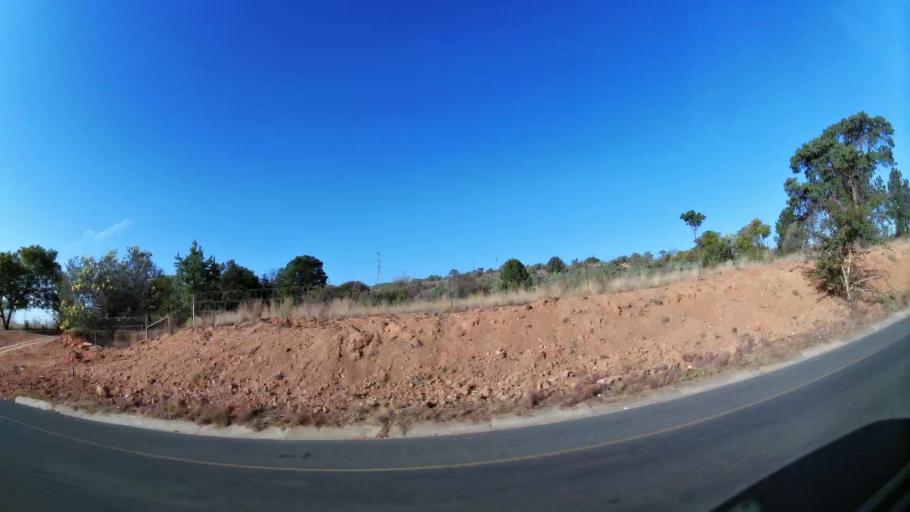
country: ZA
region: Gauteng
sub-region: West Rand District Municipality
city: Muldersdriseloop
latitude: -26.0333
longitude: 27.9095
